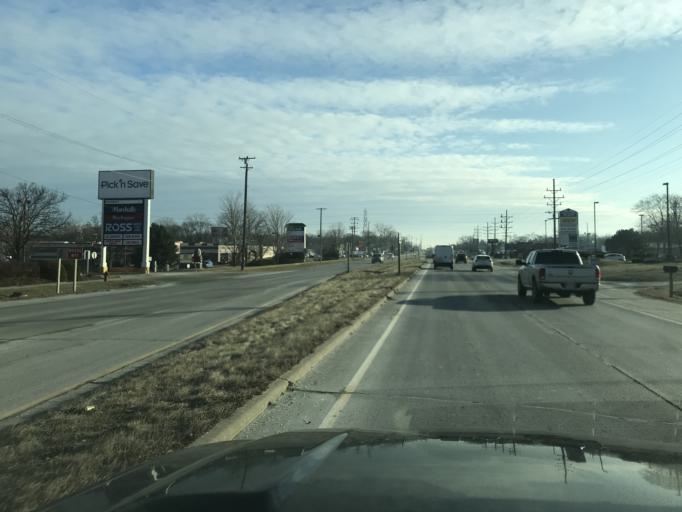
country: US
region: Wisconsin
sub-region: Kenosha County
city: Pleasant Prairie
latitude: 42.5665
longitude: -87.8790
